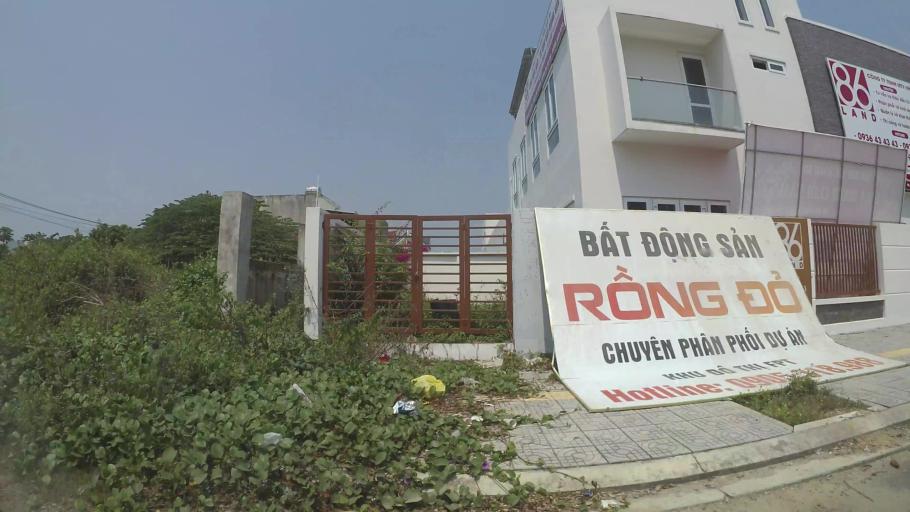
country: VN
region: Da Nang
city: Ngu Hanh Son
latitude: 15.9769
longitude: 108.2607
